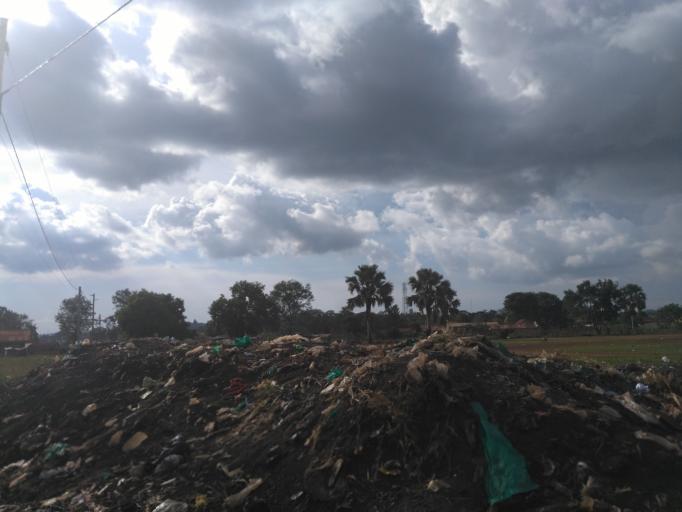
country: UG
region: Eastern Region
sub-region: Jinja District
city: Jinja
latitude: 0.4166
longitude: 33.2159
